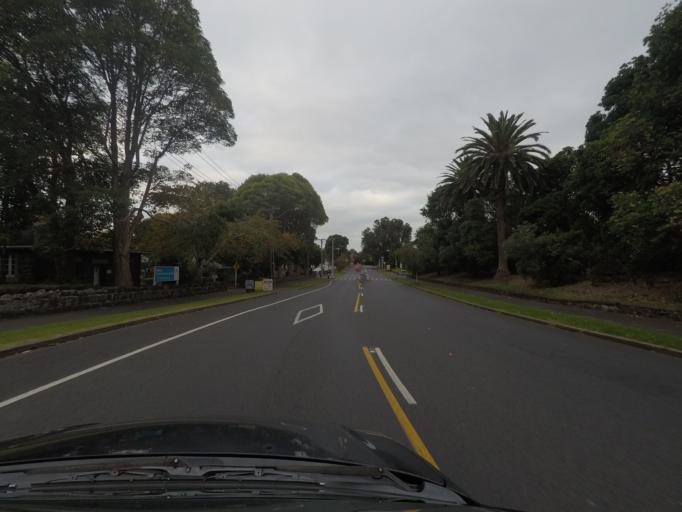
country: NZ
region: Auckland
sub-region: Auckland
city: Auckland
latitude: -36.8866
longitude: 174.7709
